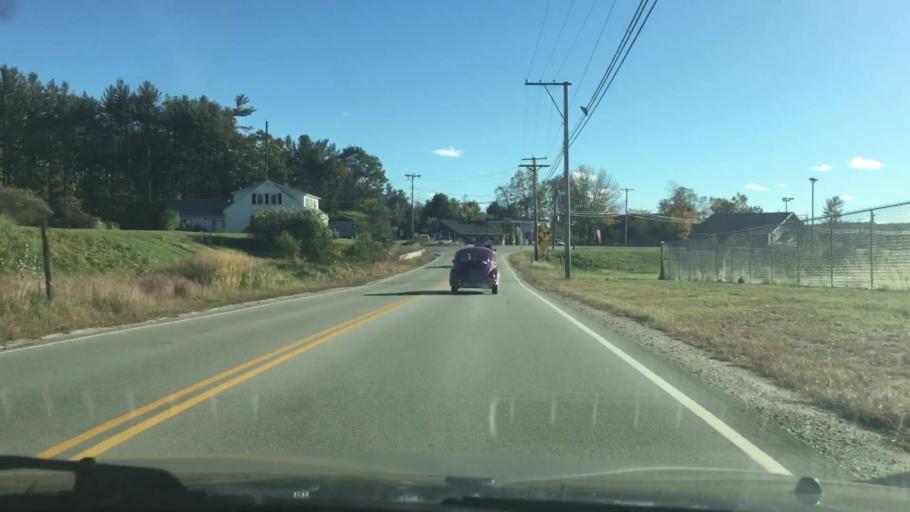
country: US
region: New Hampshire
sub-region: Cheshire County
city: Swanzey
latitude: 42.8803
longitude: -72.2703
